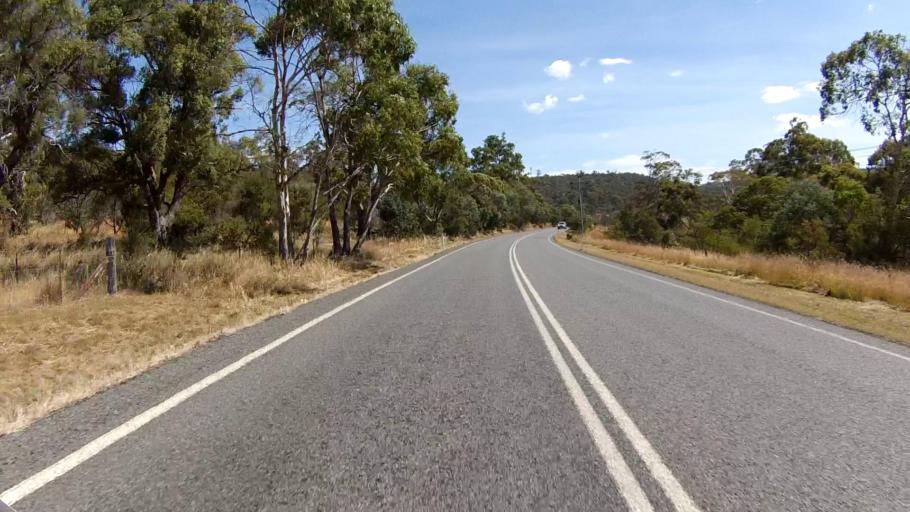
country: AU
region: Tasmania
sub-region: Sorell
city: Sorell
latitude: -42.6072
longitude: 147.6973
